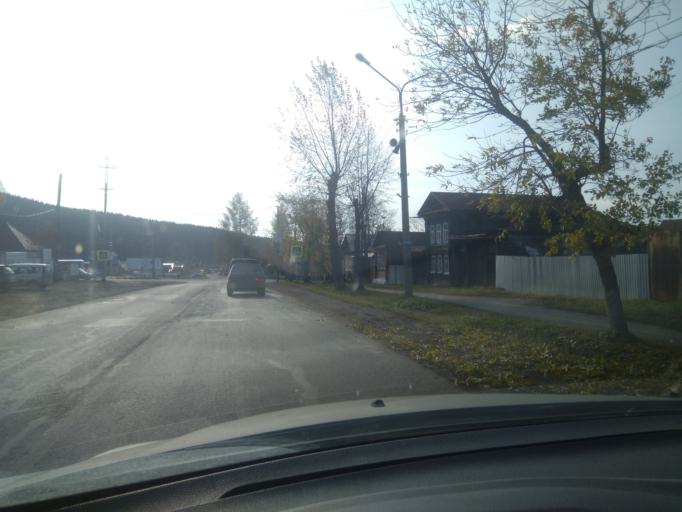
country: RU
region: Sverdlovsk
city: Nizhniye Sergi
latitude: 56.6594
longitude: 59.3010
